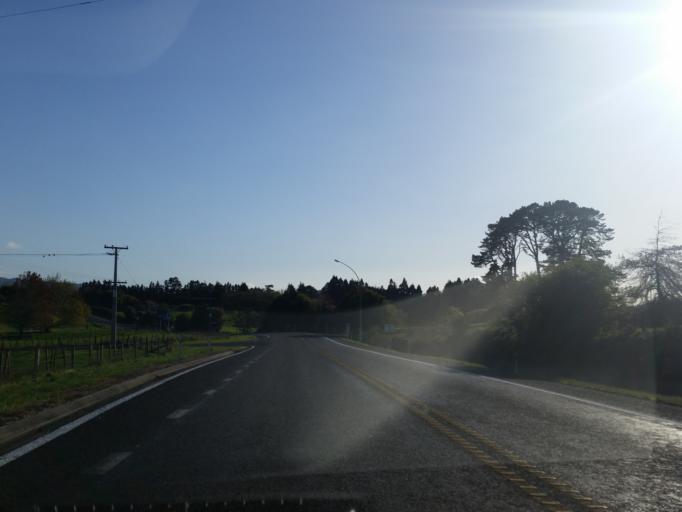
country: NZ
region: Waikato
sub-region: Hauraki District
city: Waihi
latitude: -37.4366
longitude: 175.8732
